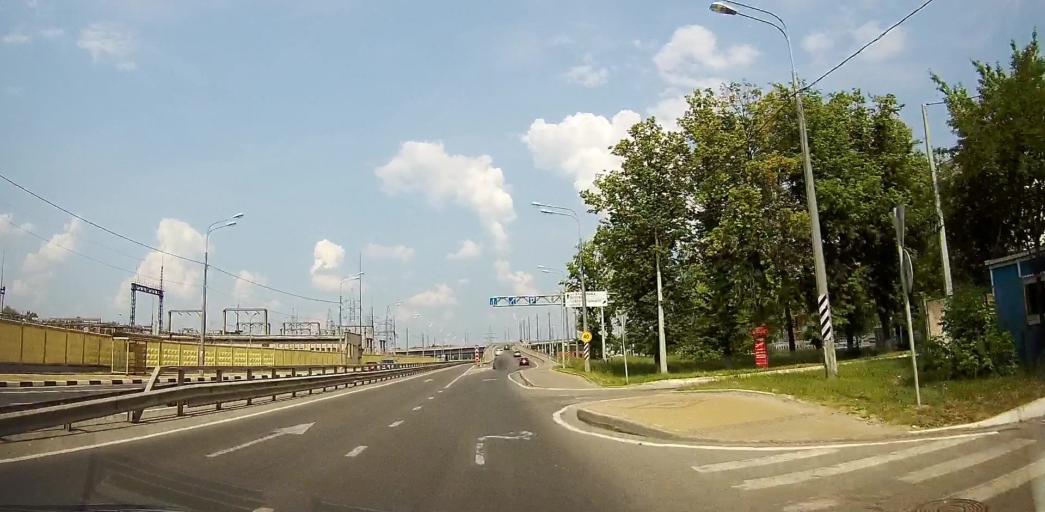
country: RU
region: Moskovskaya
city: Stupino
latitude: 54.9024
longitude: 38.0769
